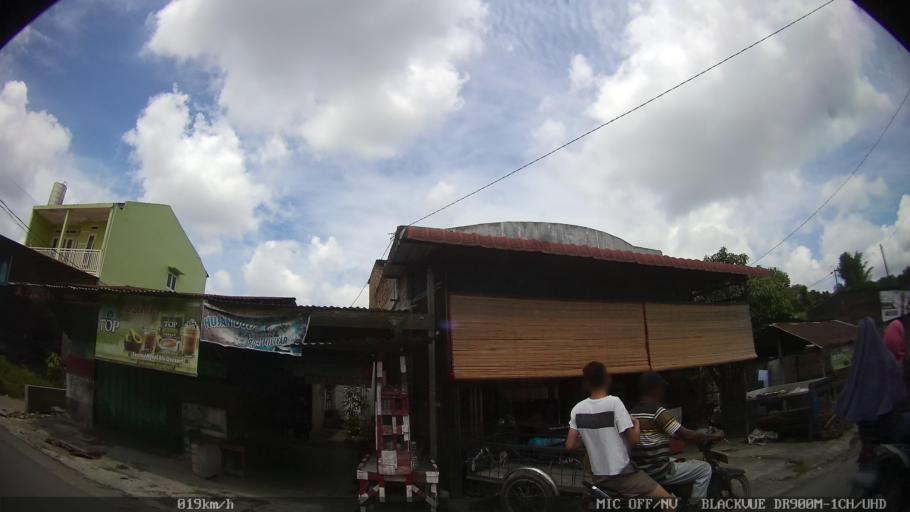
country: ID
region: North Sumatra
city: Medan
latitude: 3.6057
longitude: 98.7472
